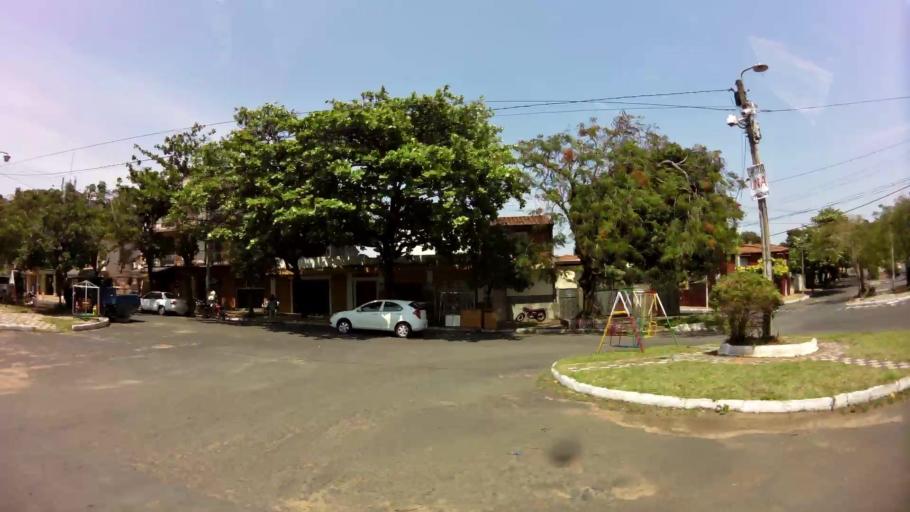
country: PY
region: Asuncion
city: Asuncion
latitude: -25.2989
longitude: -57.6412
